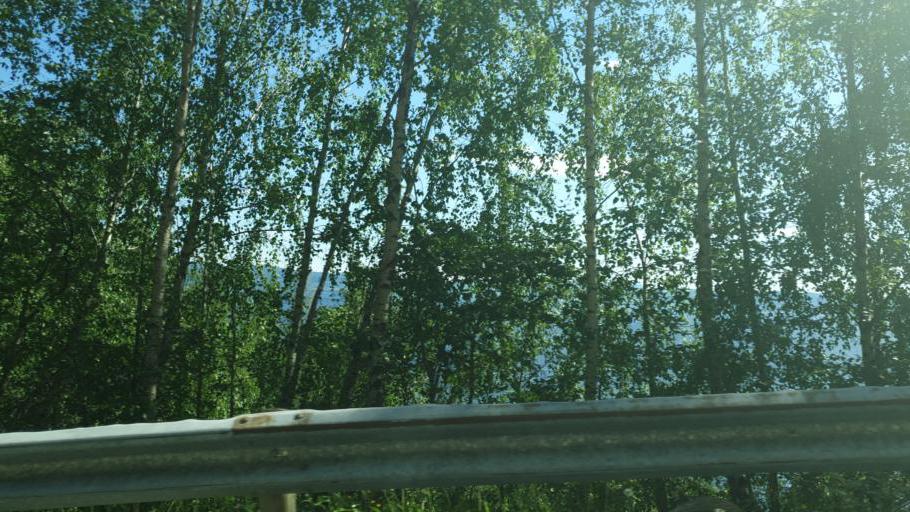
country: NO
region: Nord-Trondelag
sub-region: Frosta
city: Frosta
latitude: 63.6999
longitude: 10.7377
